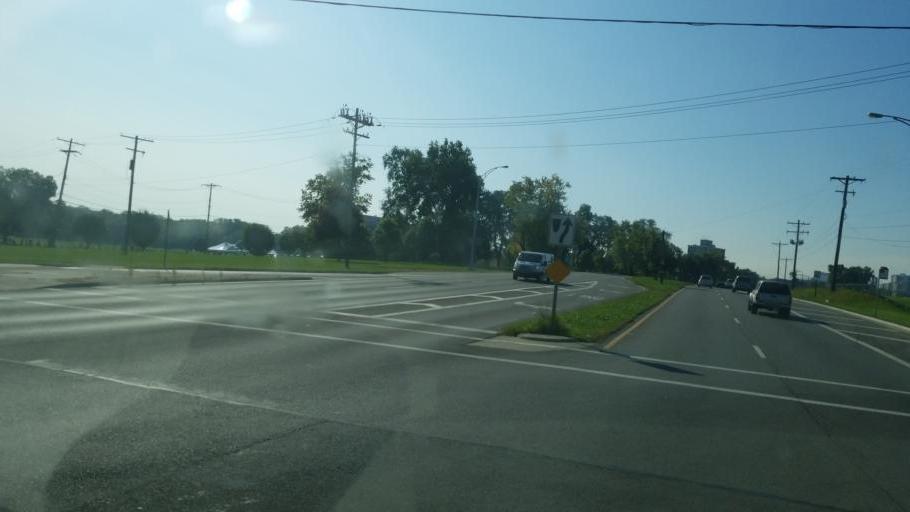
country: US
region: Ohio
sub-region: Franklin County
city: Grandview Heights
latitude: 40.0163
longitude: -83.0231
